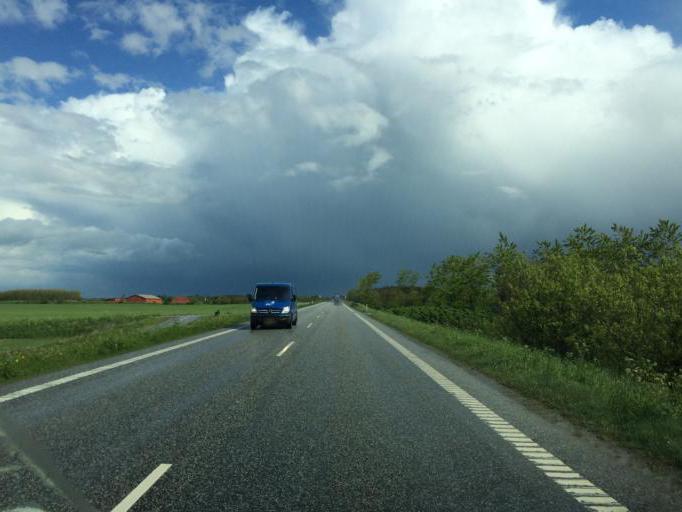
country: DK
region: Central Jutland
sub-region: Holstebro Kommune
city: Vinderup
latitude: 56.4906
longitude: 8.7864
